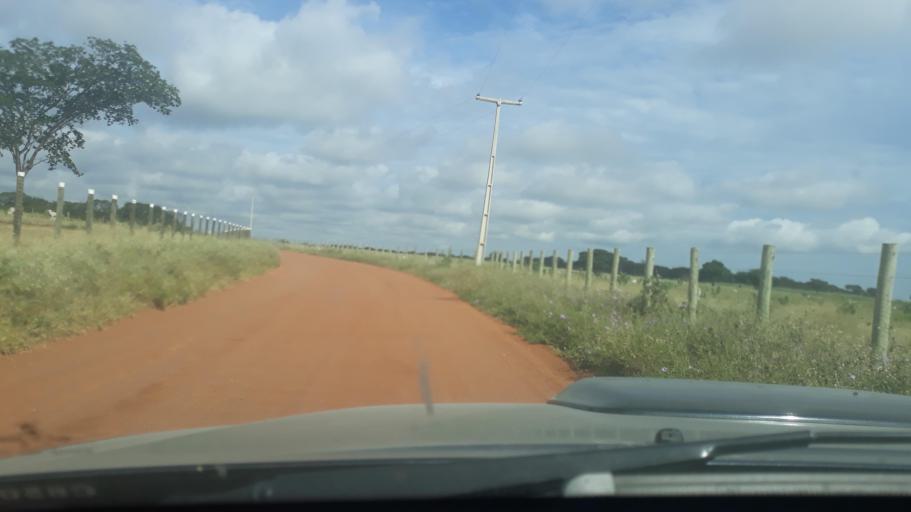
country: BR
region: Bahia
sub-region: Riacho De Santana
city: Riacho de Santana
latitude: -13.9007
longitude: -42.8882
